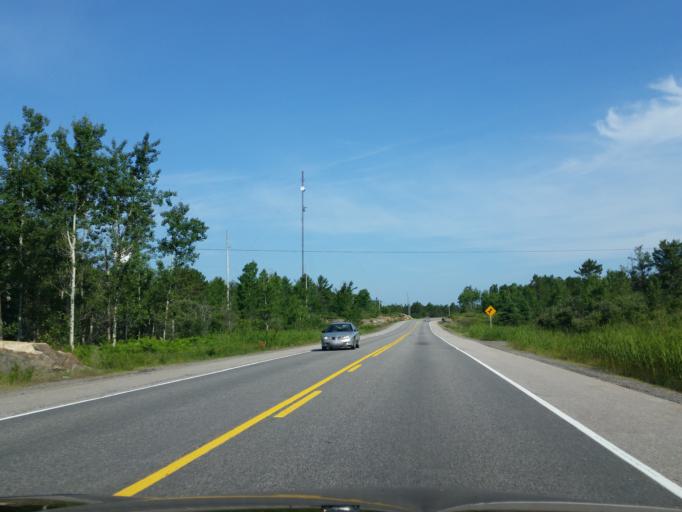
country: CA
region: Ontario
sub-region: Parry Sound District
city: Parry Sound
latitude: 45.7917
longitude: -80.5298
